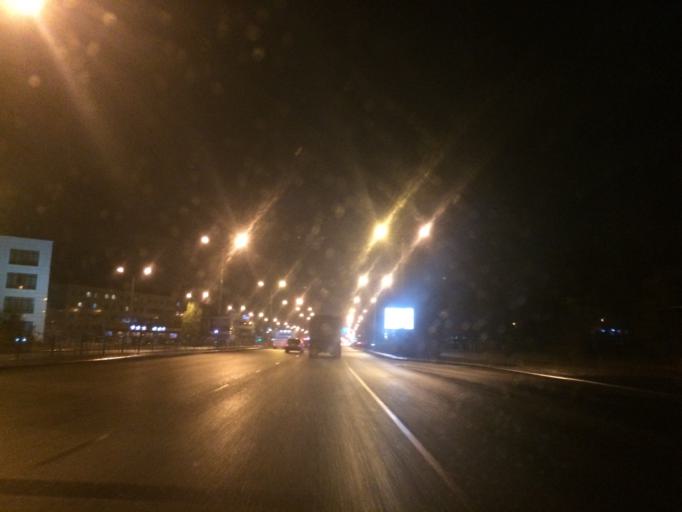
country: KZ
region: Astana Qalasy
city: Astana
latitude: 51.1768
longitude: 71.3930
